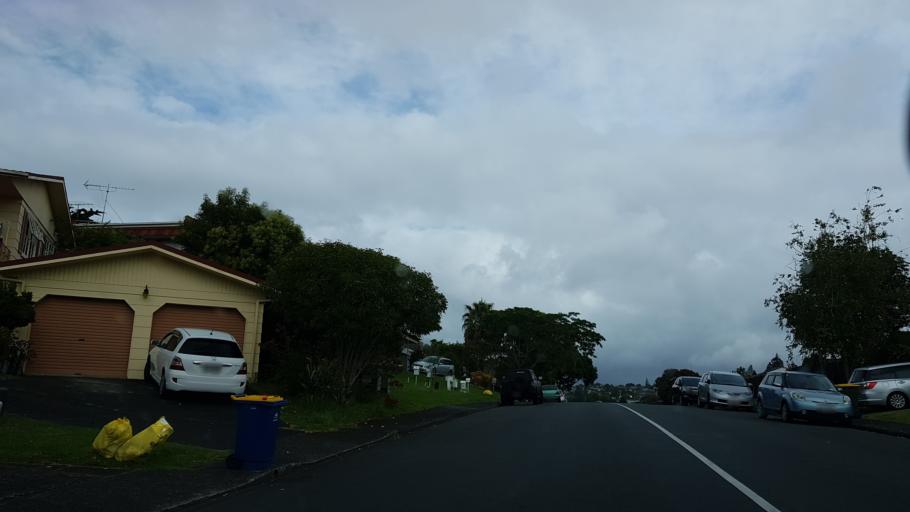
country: NZ
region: Auckland
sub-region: Auckland
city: North Shore
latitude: -36.7870
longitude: 174.7340
